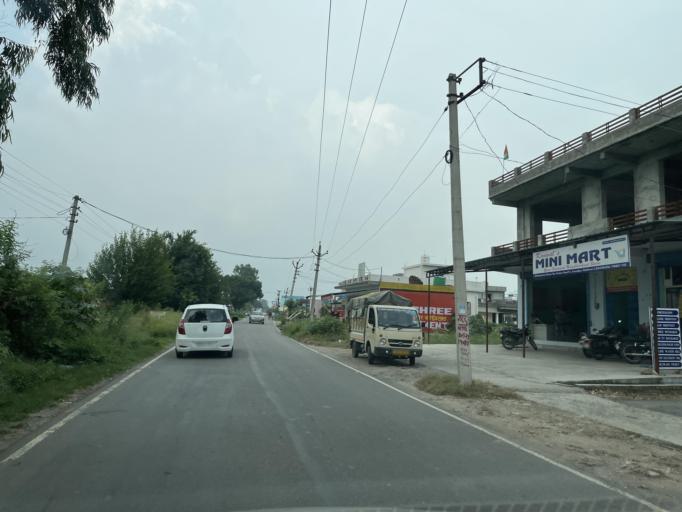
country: IN
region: Uttarakhand
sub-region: Naini Tal
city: Haldwani
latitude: 29.1845
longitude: 79.4758
